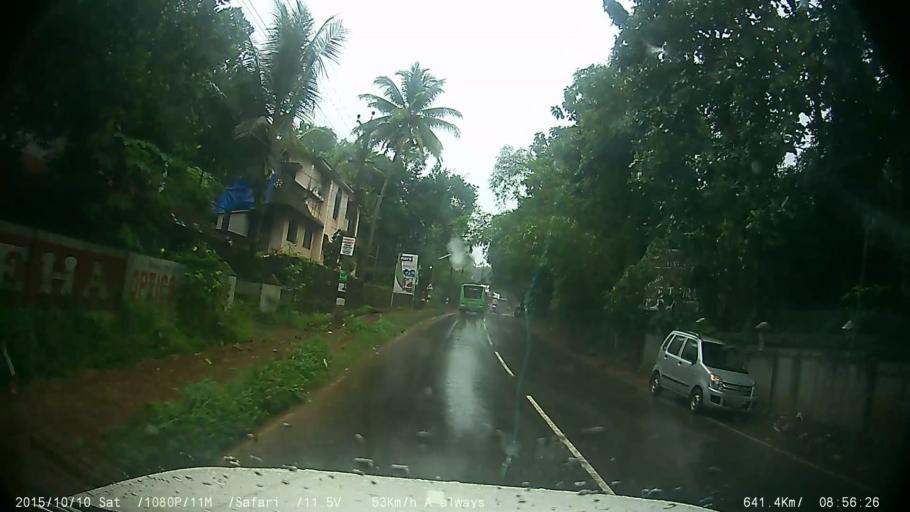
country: IN
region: Kerala
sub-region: Kottayam
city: Palackattumala
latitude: 9.6946
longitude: 76.5506
